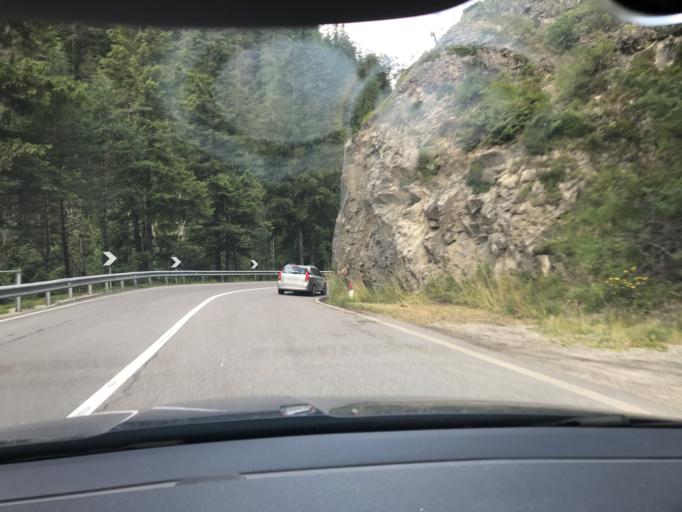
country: IT
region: Trentino-Alto Adige
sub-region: Bolzano
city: San Martino in Badia
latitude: 46.6706
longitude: 11.9051
